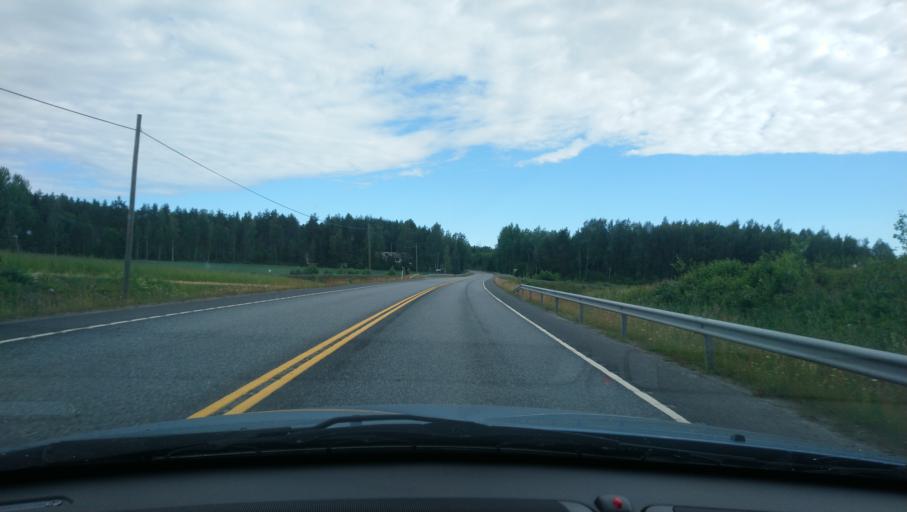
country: FI
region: Uusimaa
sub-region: Porvoo
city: Porvoo
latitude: 60.4208
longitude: 25.5790
